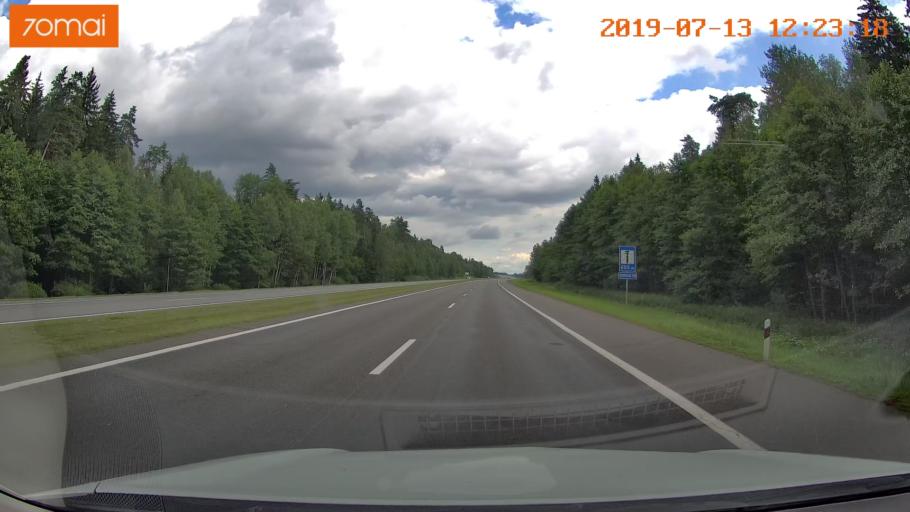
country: BY
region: Minsk
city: Hatava
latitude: 53.7535
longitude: 27.6501
